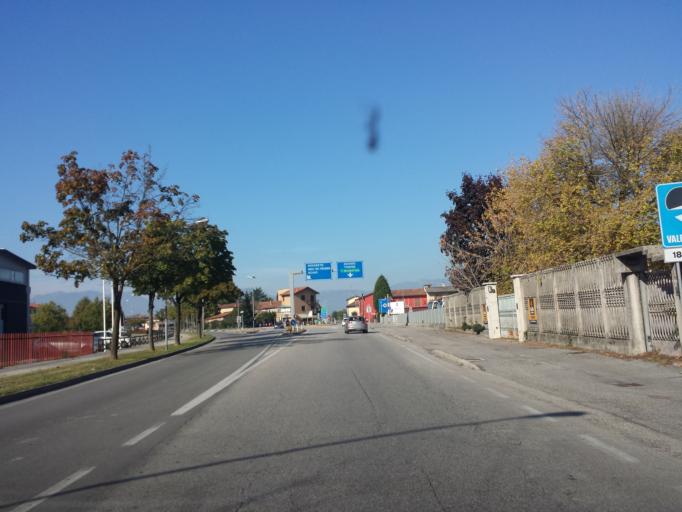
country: IT
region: Veneto
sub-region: Provincia di Vicenza
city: Motta
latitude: 45.6023
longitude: 11.4941
